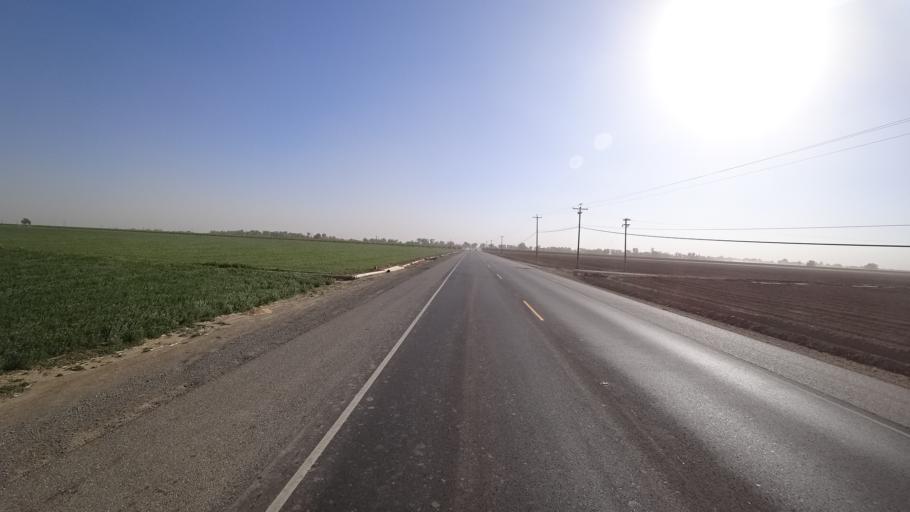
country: US
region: California
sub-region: Yolo County
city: Woodland
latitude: 38.7382
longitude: -121.7295
